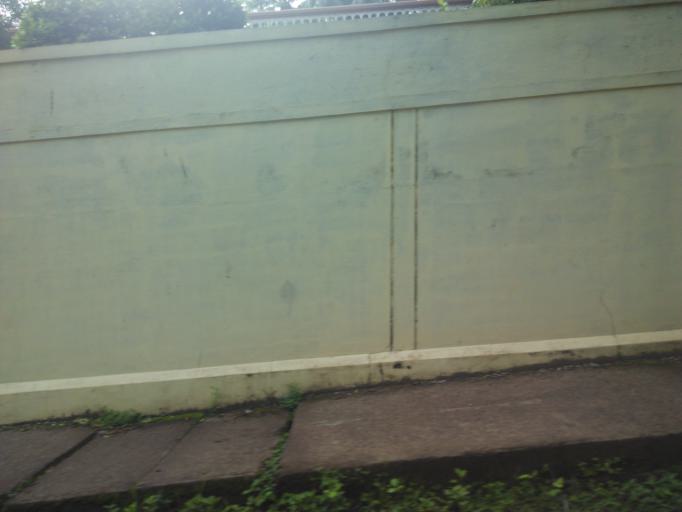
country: IN
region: Kerala
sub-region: Kozhikode
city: Kozhikode
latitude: 11.2937
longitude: 75.8129
